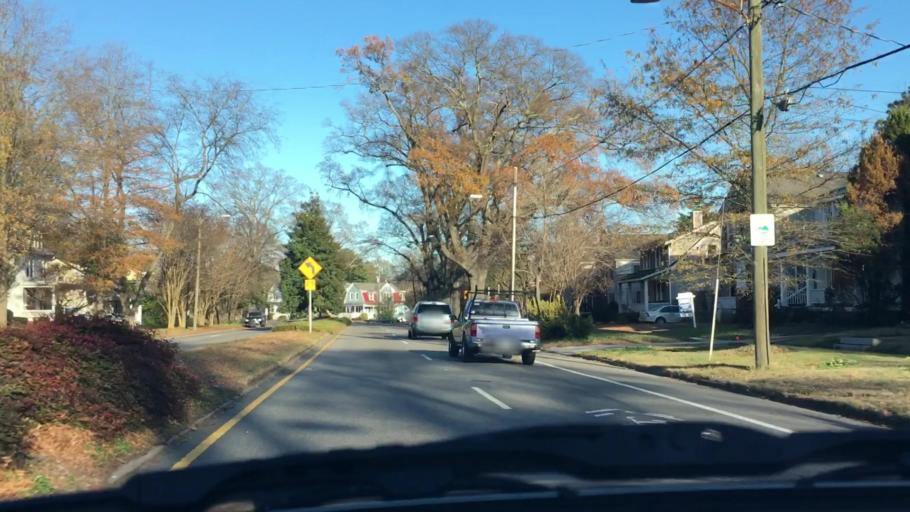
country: US
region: Virginia
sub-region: City of Norfolk
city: Norfolk
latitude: 36.8751
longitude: -76.2695
